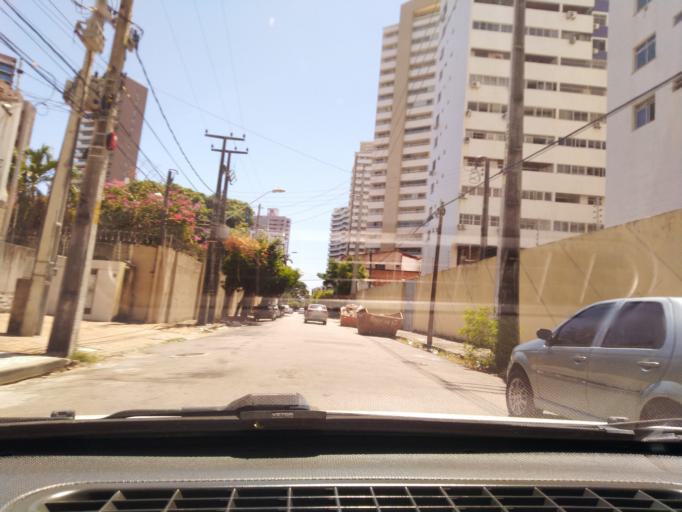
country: BR
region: Ceara
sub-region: Fortaleza
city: Fortaleza
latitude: -3.7443
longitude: -38.4757
